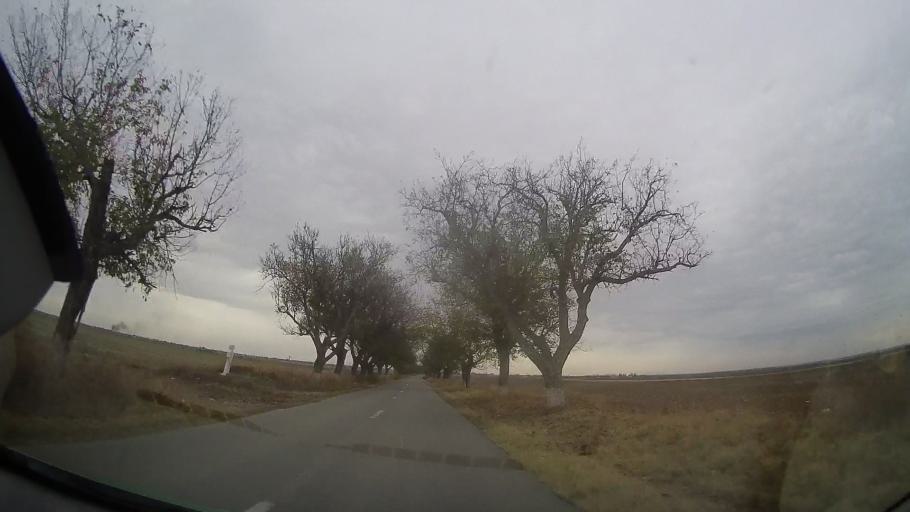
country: RO
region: Prahova
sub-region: Comuna Fantanele
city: Fantanele
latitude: 45.0145
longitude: 26.4066
